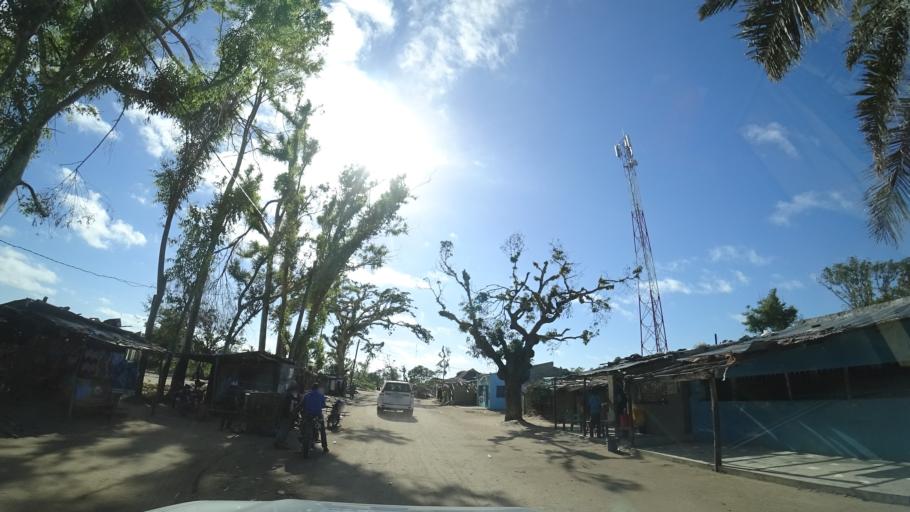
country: MZ
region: Sofala
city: Beira
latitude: -19.7161
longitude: 35.0074
